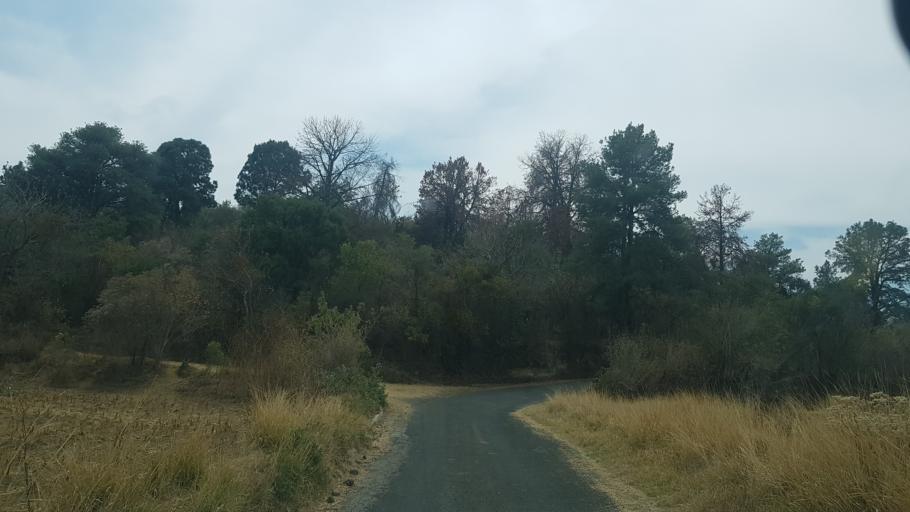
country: MX
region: Puebla
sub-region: Atzitzihuacan
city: Santiago Atzitzihuacan
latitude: 18.8432
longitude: -98.6104
